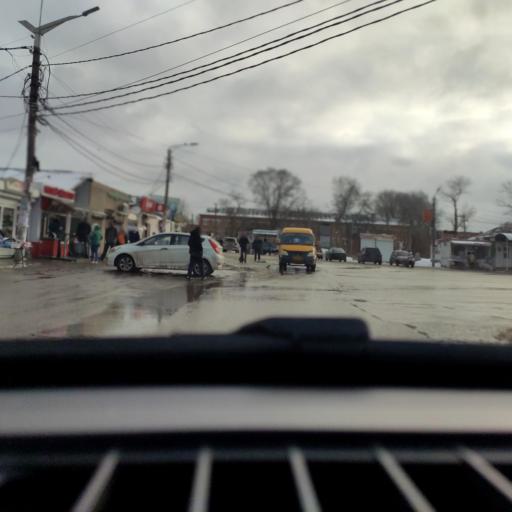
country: RU
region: Voronezj
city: Semiluki
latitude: 51.6829
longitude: 39.0356
